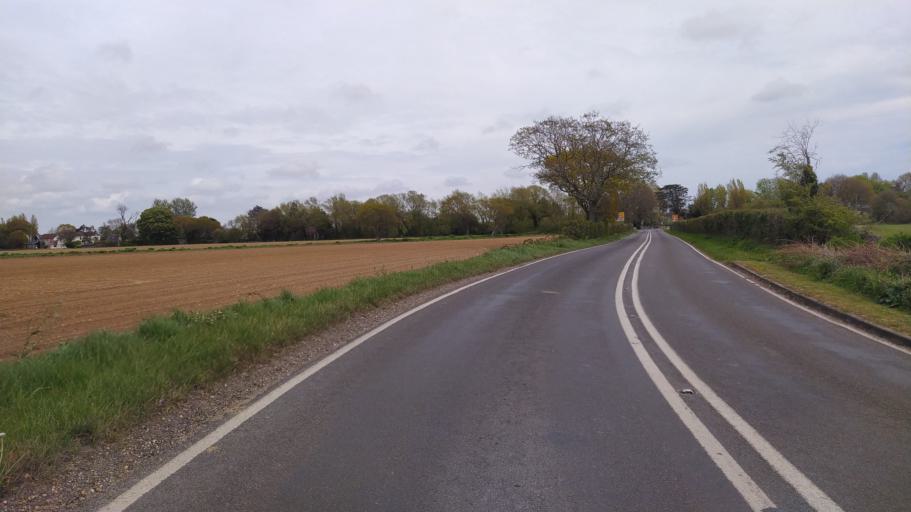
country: GB
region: England
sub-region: West Sussex
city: Birdham
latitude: 50.7788
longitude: -0.8468
